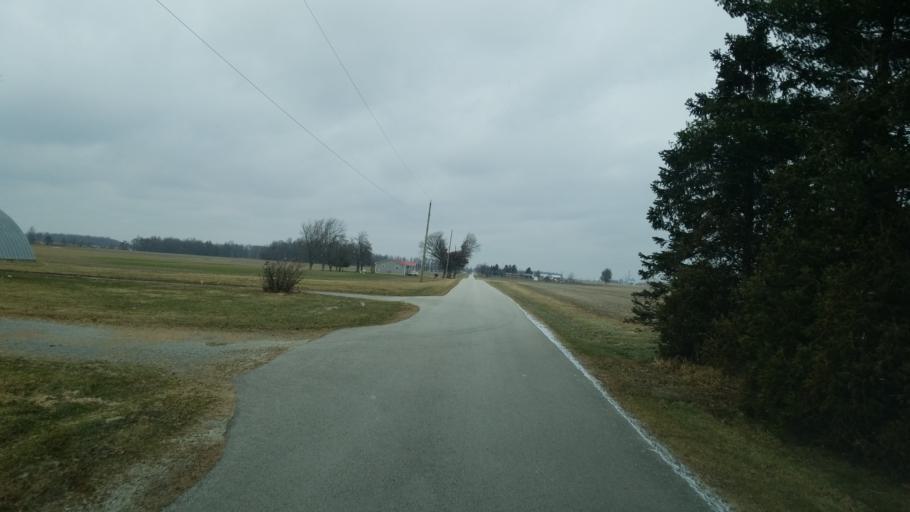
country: US
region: Ohio
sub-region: Hardin County
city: Forest
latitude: 40.7632
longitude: -83.4777
